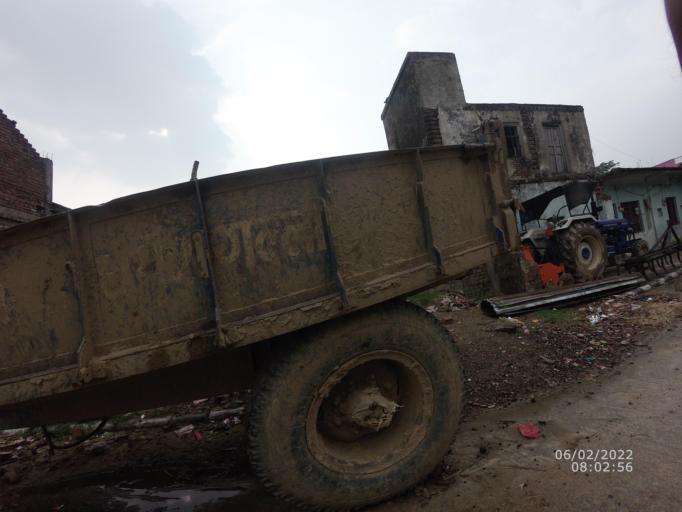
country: NP
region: Western Region
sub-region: Lumbini Zone
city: Bhairahawa
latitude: 27.4798
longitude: 83.4750
